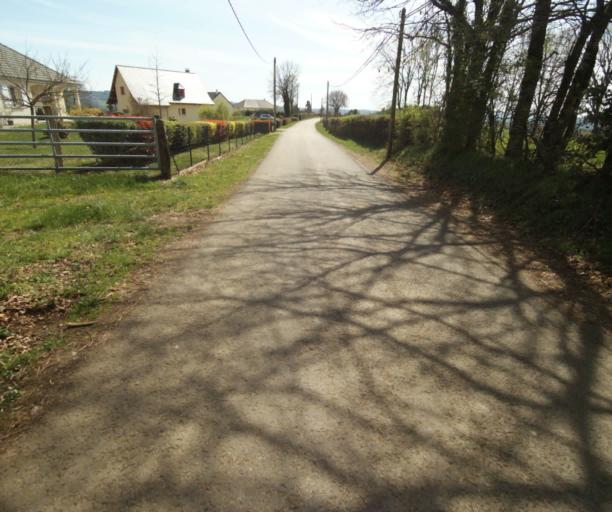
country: FR
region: Limousin
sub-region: Departement de la Correze
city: Naves
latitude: 45.3699
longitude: 1.8022
